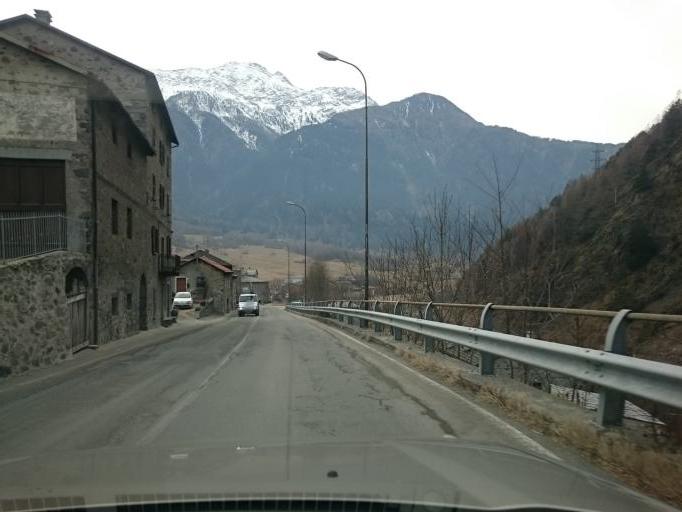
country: IT
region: Lombardy
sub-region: Provincia di Sondrio
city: Sondalo
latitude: 46.3353
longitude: 10.3494
